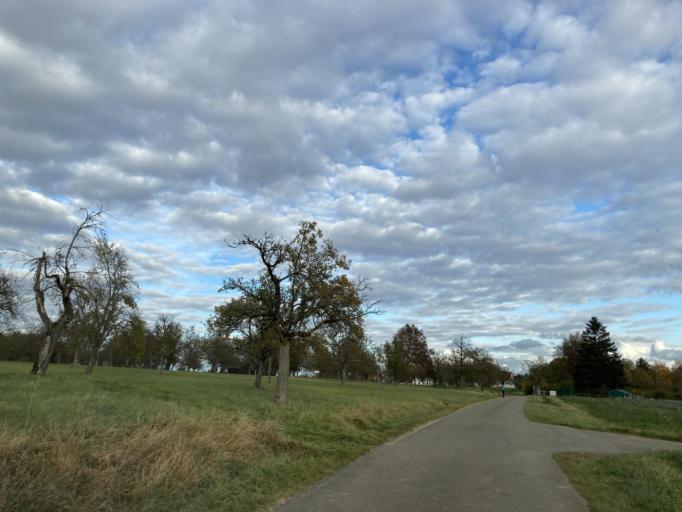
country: DE
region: Baden-Wuerttemberg
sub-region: Tuebingen Region
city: Gomaringen
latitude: 48.4729
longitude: 9.0758
